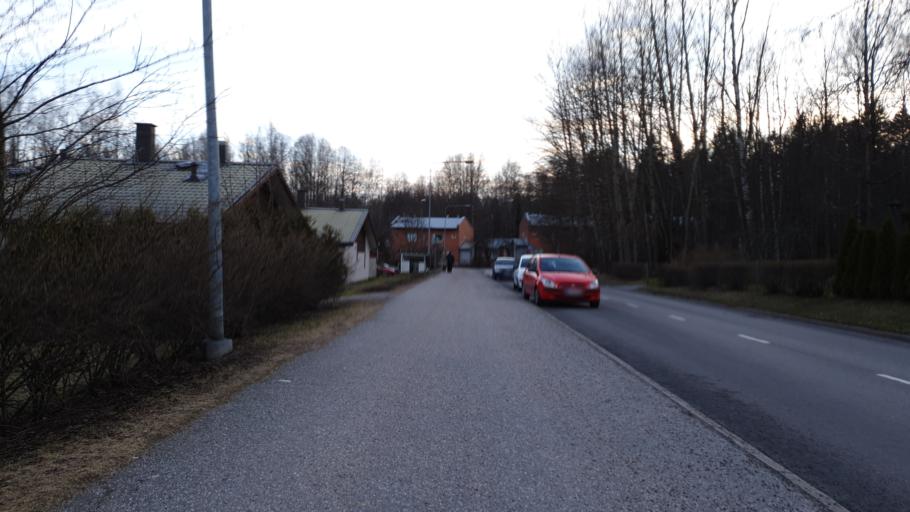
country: FI
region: Uusimaa
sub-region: Helsinki
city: Vantaa
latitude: 60.3090
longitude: 25.0053
